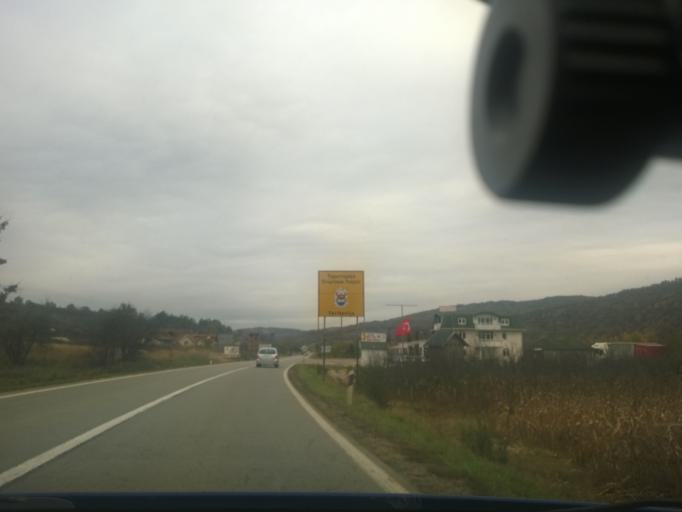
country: RS
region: Central Serbia
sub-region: Pirotski Okrug
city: Dimitrovgrad
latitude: 43.0256
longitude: 22.7219
